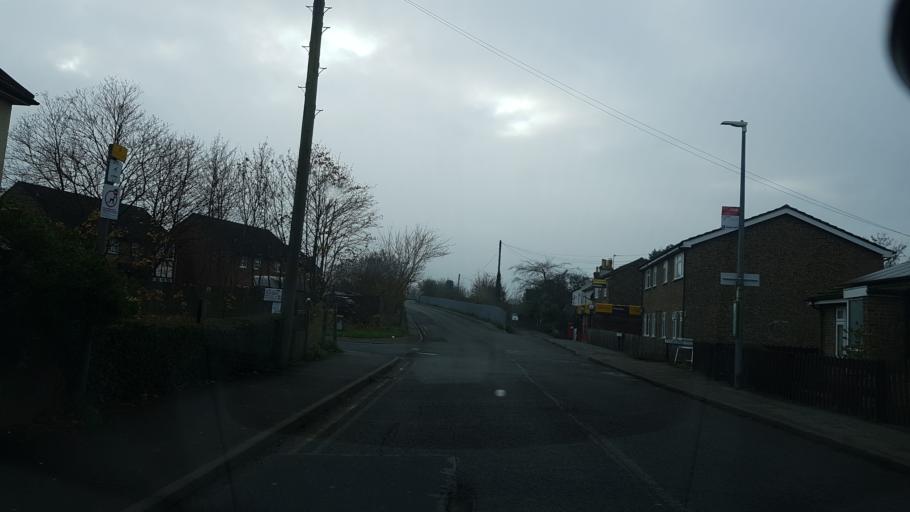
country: GB
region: England
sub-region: Central Bedfordshire
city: Biggleswade
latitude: 52.0923
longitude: -0.2593
